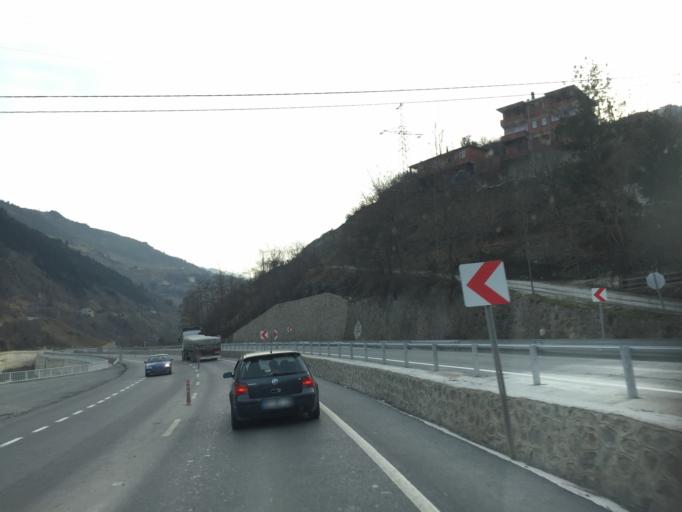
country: TR
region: Trabzon
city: Macka
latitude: 40.7999
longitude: 39.5848
